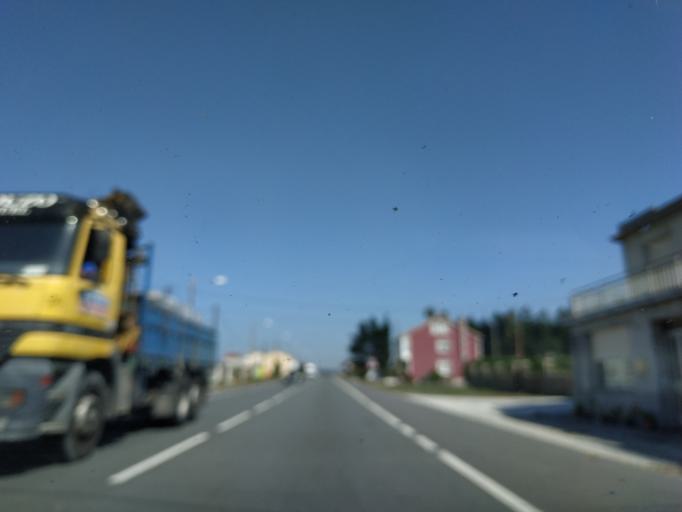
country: ES
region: Galicia
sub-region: Provincia da Coruna
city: Laracha
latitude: 43.2459
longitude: -8.6252
